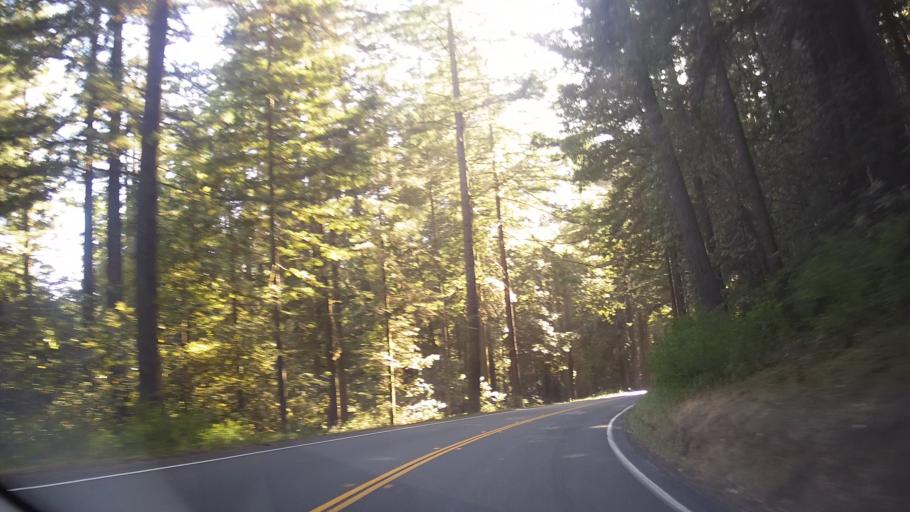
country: US
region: California
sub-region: Mendocino County
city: Brooktrails
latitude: 39.3464
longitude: -123.5631
